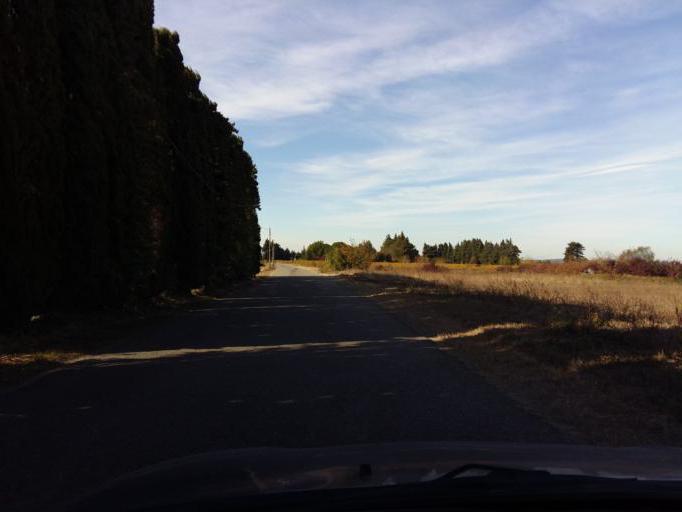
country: FR
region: Provence-Alpes-Cote d'Azur
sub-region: Departement du Vaucluse
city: Serignan-du-Comtat
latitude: 44.1672
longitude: 4.8510
